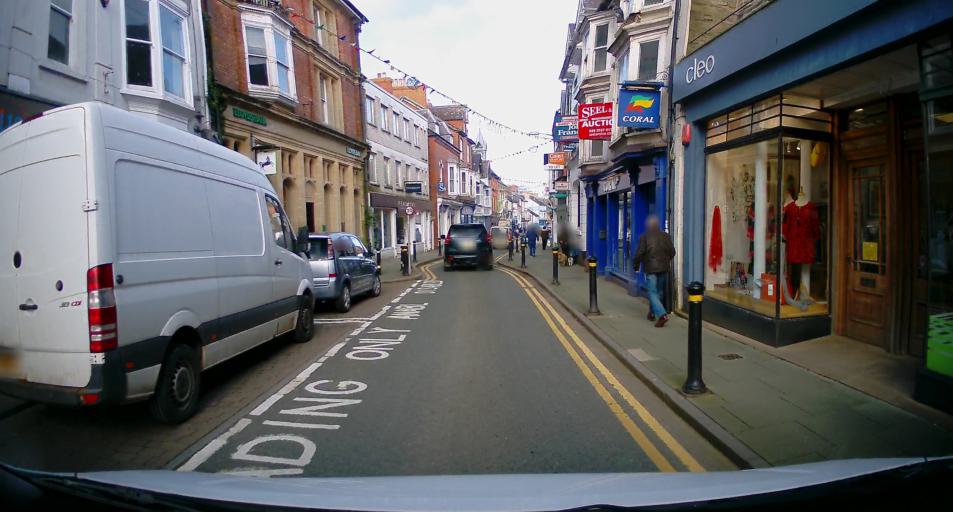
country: GB
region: Wales
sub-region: County of Ceredigion
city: Cardigan
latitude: 52.0829
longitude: -4.6612
